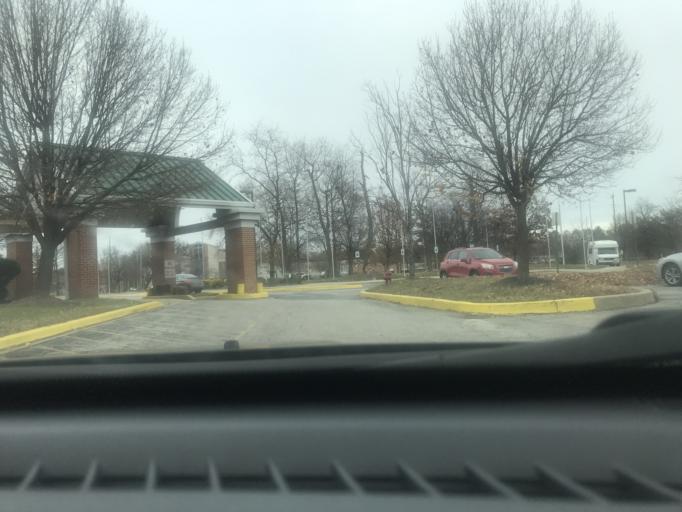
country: US
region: Maryland
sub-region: Prince George's County
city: Oxon Hill
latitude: 38.7979
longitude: -76.9798
